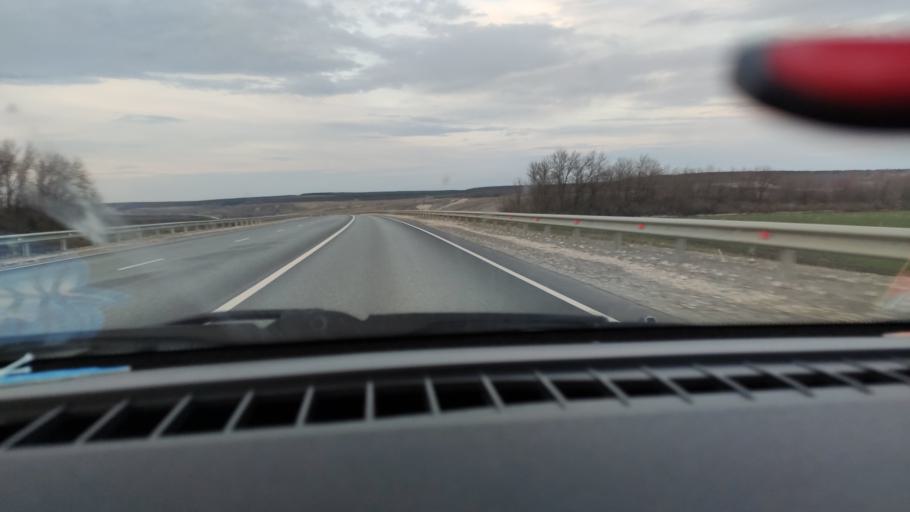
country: RU
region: Saratov
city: Yelshanka
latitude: 51.8407
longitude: 46.4766
